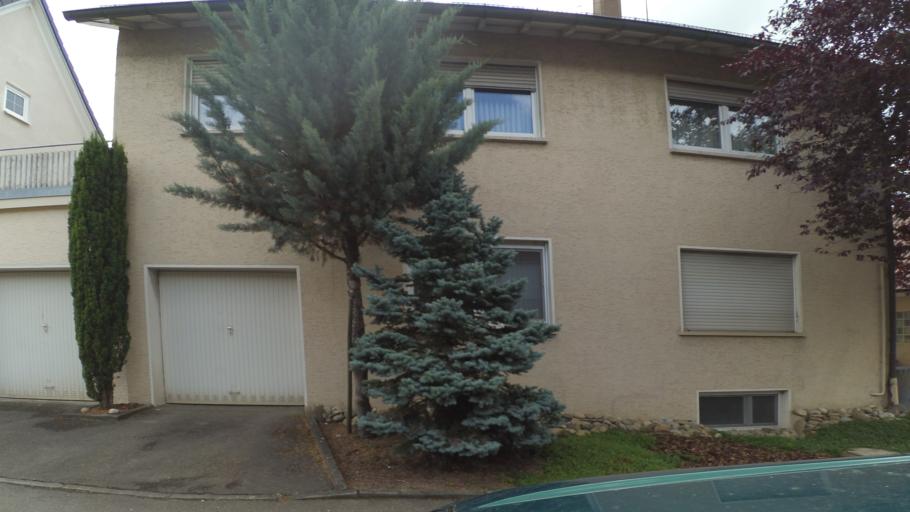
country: DE
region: Baden-Wuerttemberg
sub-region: Regierungsbezirk Stuttgart
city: Ottenbach
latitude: 48.7342
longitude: 9.7477
